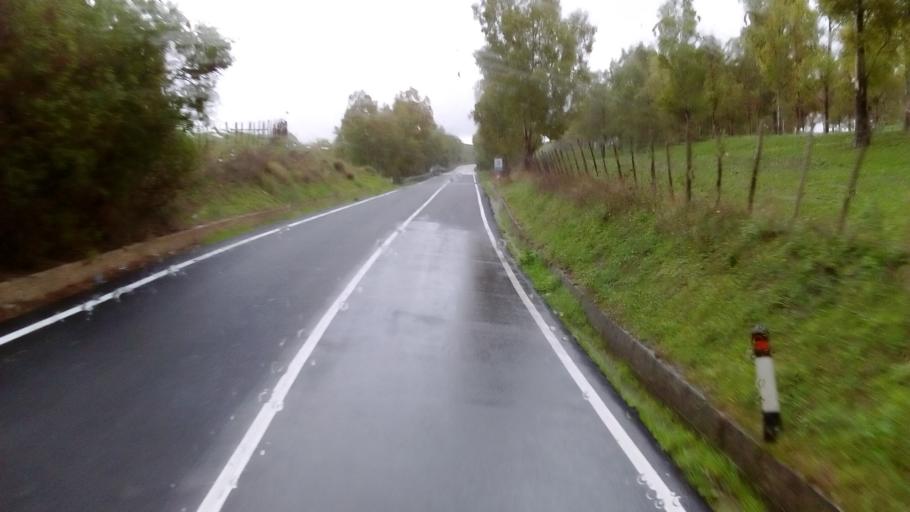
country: IT
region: Sicily
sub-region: Enna
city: Pietraperzia
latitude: 37.4725
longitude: 14.1676
